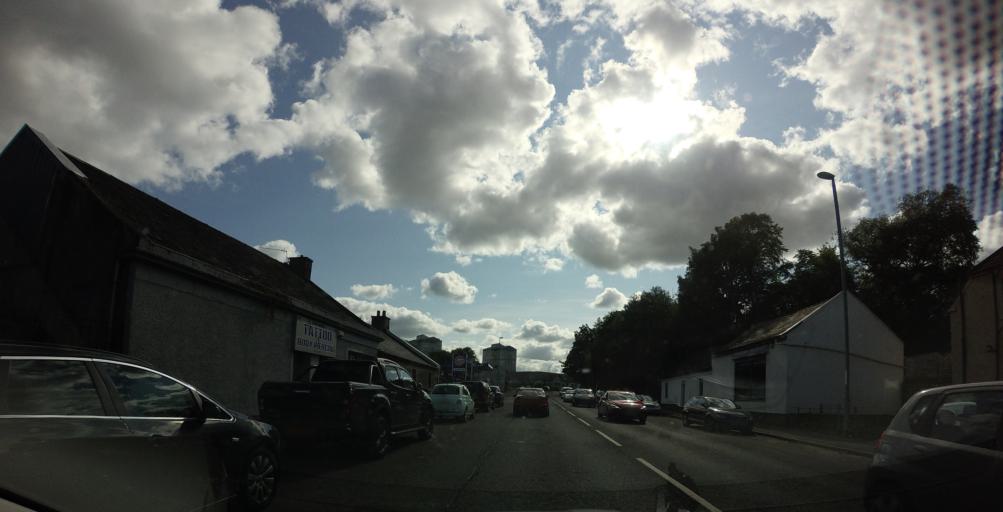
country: GB
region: Scotland
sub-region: North Lanarkshire
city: Coatbridge
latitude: 55.8566
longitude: -4.0462
